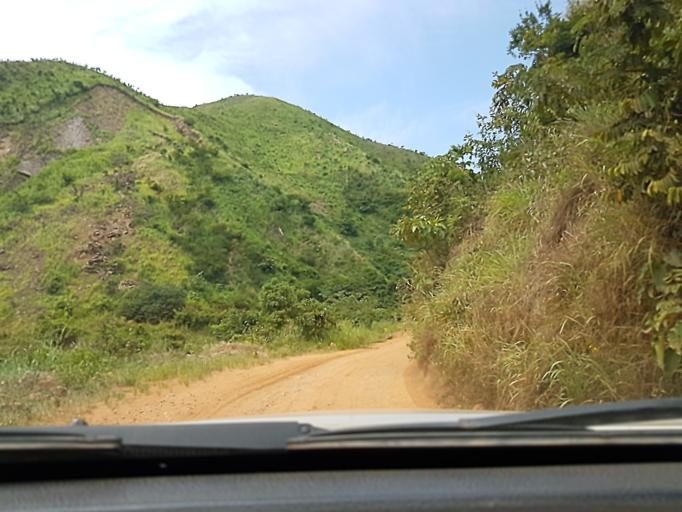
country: RW
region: Western Province
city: Cyangugu
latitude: -2.7066
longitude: 28.9440
